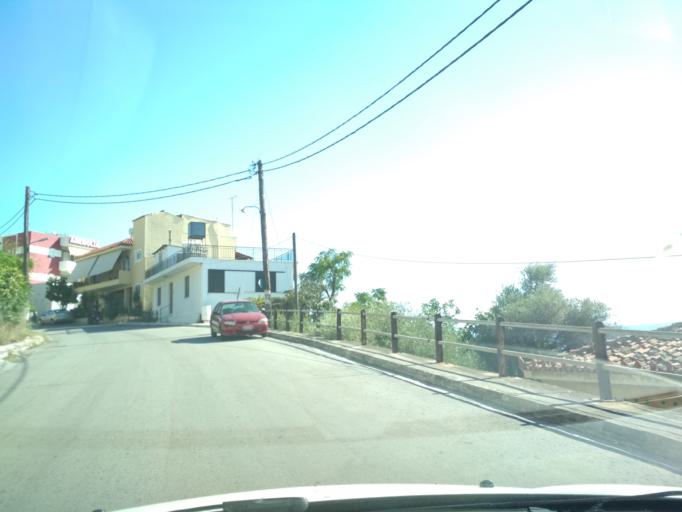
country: GR
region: Central Greece
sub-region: Nomos Evvoias
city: Oreoi
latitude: 38.8537
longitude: 23.0520
